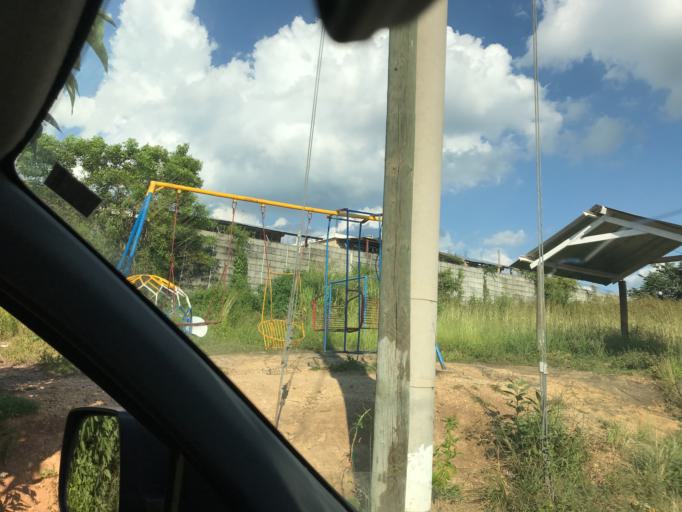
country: GT
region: Guatemala
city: Petapa
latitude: 14.4939
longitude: -90.5498
